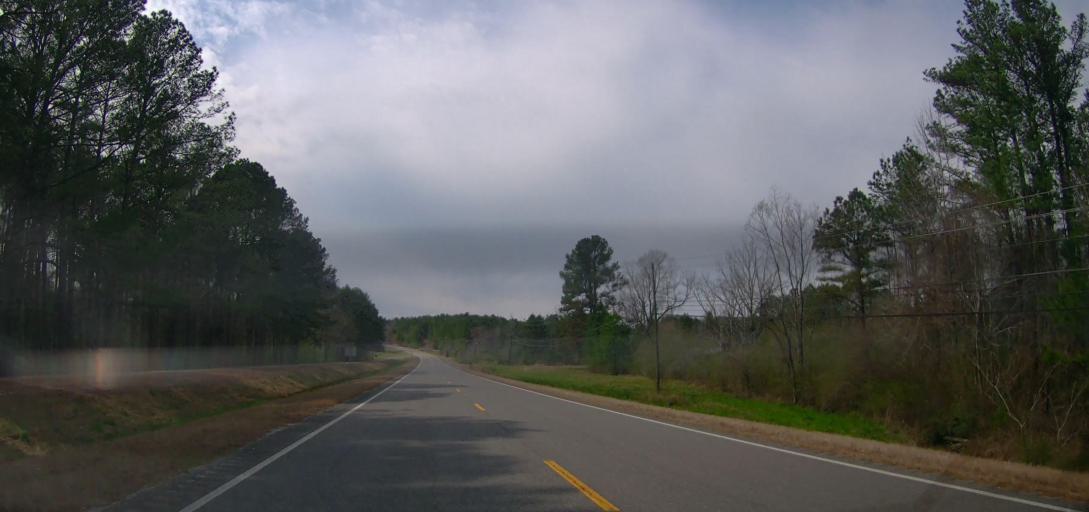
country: US
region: Alabama
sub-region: Walker County
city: Carbon Hill
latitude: 33.9213
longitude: -87.5844
